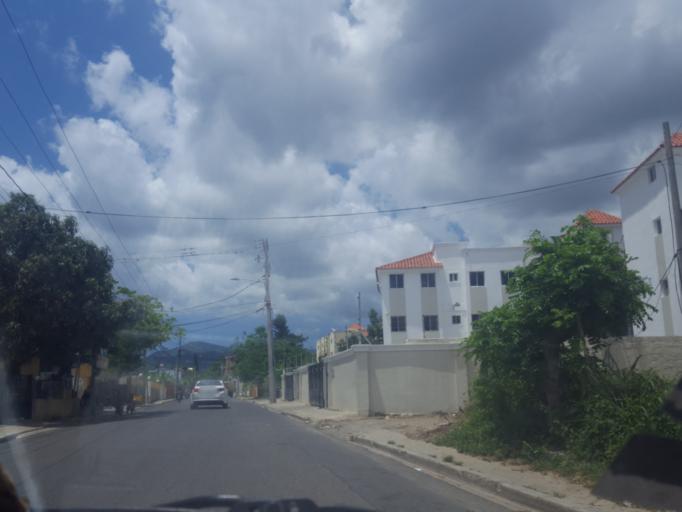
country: DO
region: Santiago
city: Santiago de los Caballeros
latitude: 19.4746
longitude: -70.6621
